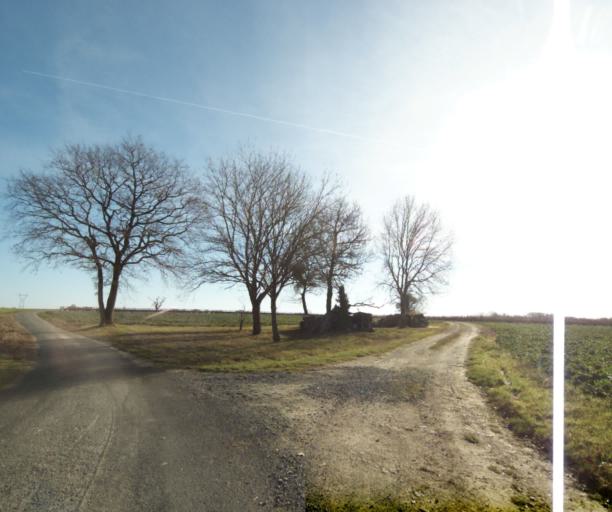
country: FR
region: Poitou-Charentes
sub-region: Departement de la Charente-Maritime
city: Cherac
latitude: 45.7442
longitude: -0.4896
